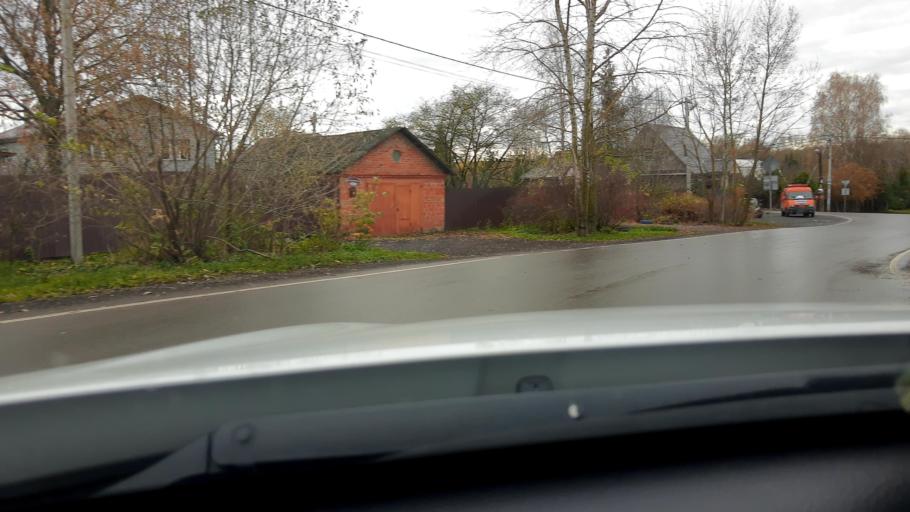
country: RU
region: Moskovskaya
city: Annino
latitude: 55.5652
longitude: 37.2365
